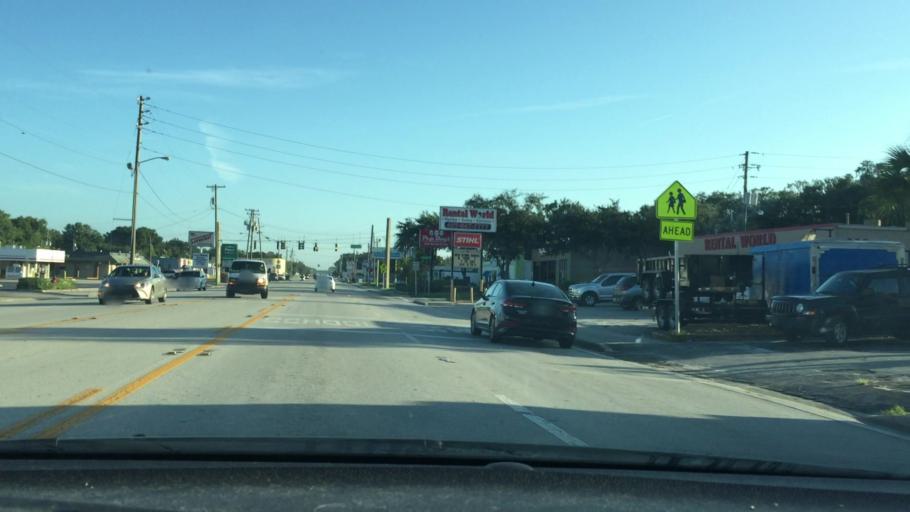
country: US
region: Florida
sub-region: Osceola County
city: Kissimmee
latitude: 28.3075
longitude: -81.4037
